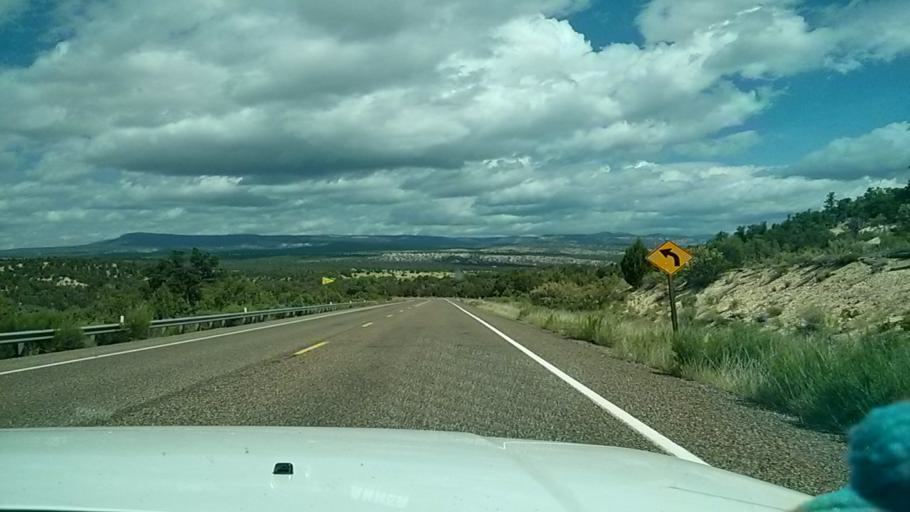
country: US
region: Utah
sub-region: Kane County
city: Kanab
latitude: 37.2012
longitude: -112.6705
